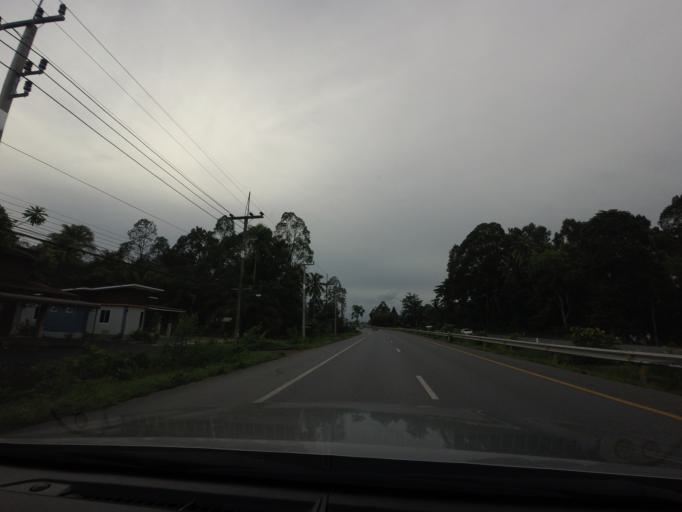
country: TH
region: Nakhon Si Thammarat
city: Chian Yai
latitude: 8.1016
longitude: 100.1080
